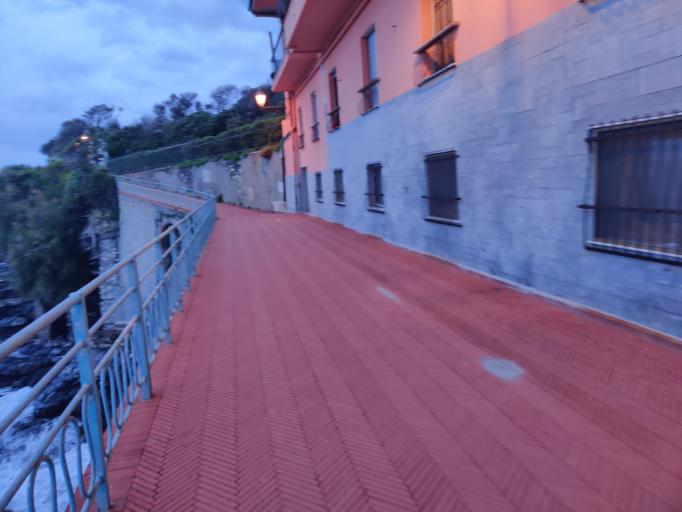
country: IT
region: Liguria
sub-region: Provincia di Genova
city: Bogliasco
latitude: 44.3800
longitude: 9.0493
